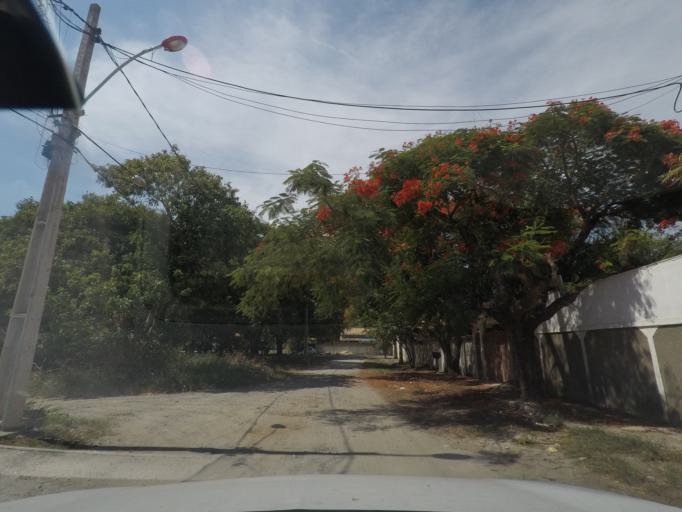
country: BR
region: Rio de Janeiro
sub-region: Marica
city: Marica
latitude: -22.9550
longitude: -42.9658
